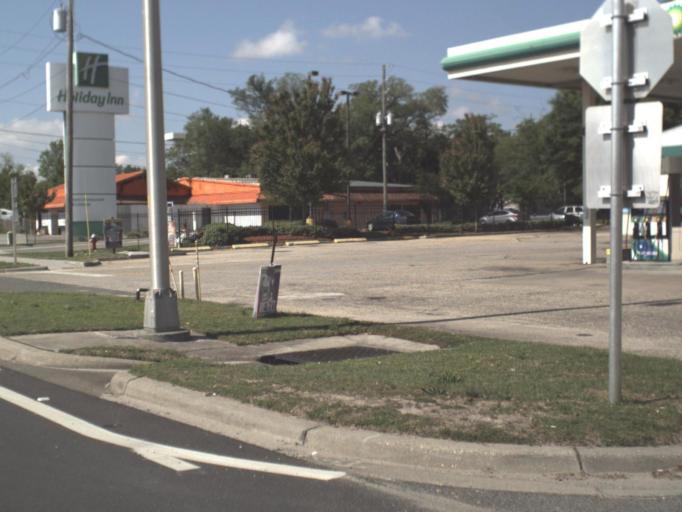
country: US
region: Florida
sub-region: Escambia County
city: Ferry Pass
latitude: 30.5063
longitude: -87.2217
